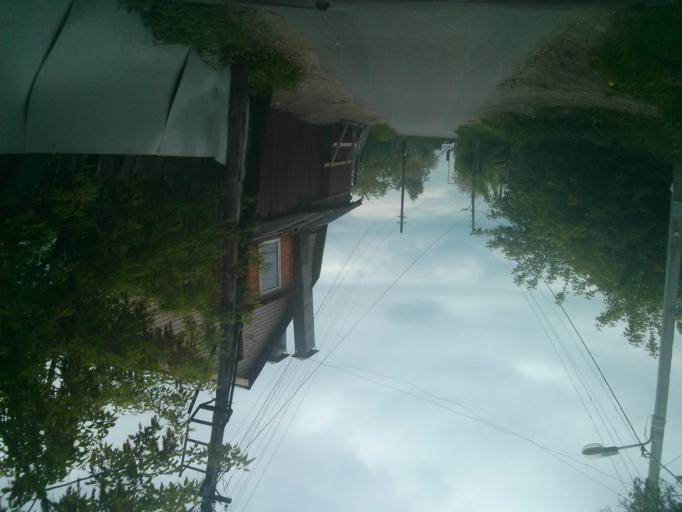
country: RU
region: Nizjnij Novgorod
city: Afonino
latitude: 56.2968
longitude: 44.0994
